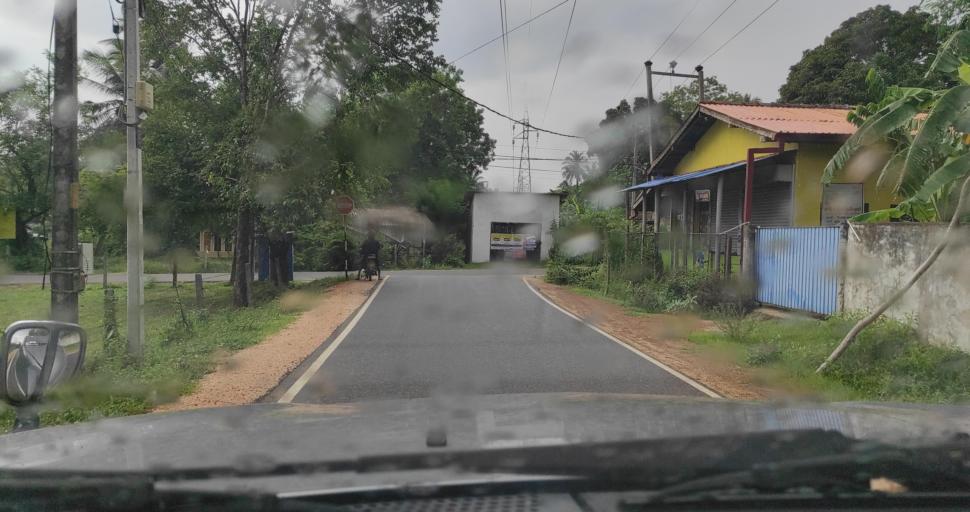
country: LK
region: Eastern Province
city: Trincomalee
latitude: 8.3671
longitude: 81.0087
